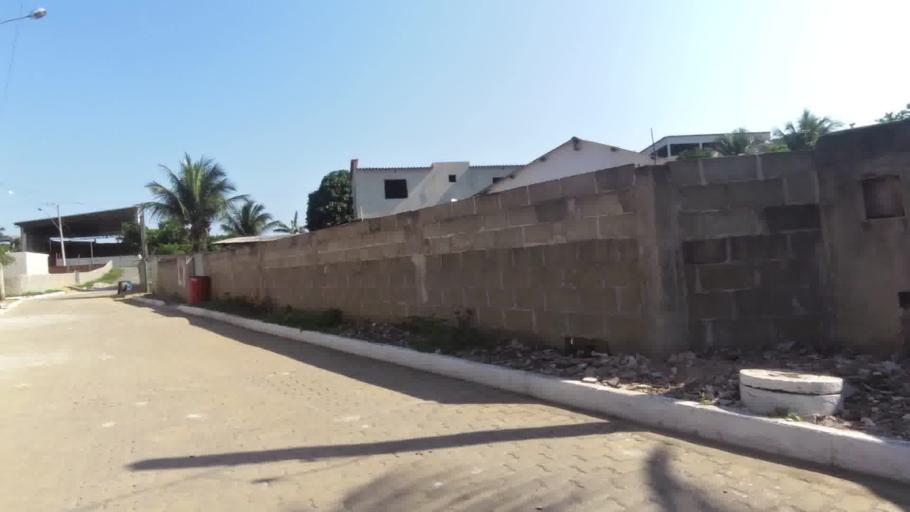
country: BR
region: Espirito Santo
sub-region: Piuma
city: Piuma
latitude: -20.8087
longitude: -40.7382
